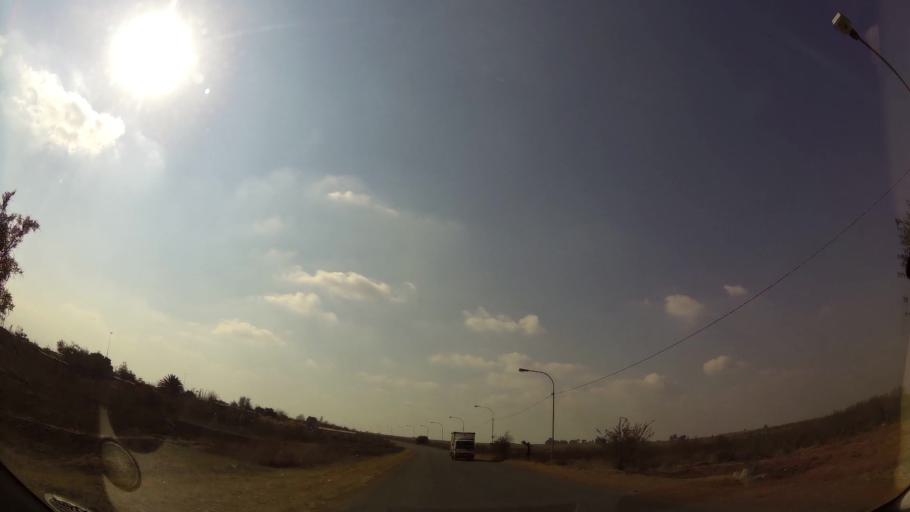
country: ZA
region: Gauteng
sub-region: Ekurhuleni Metropolitan Municipality
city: Springs
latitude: -26.1328
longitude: 28.4805
